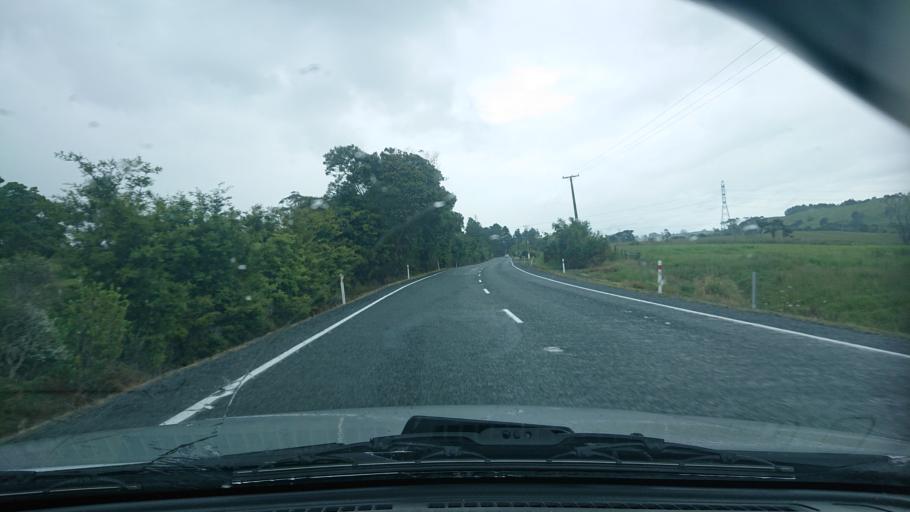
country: NZ
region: Auckland
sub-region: Auckland
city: Wellsford
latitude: -36.3244
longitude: 174.4782
